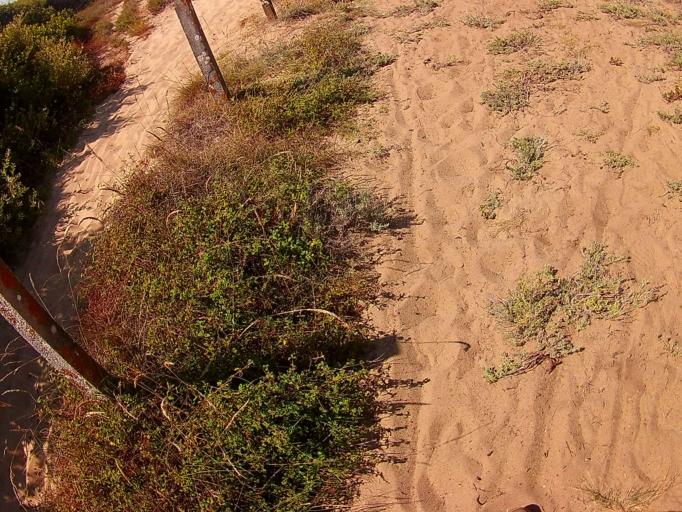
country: FR
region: Aquitaine
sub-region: Departement des Landes
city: Labenne
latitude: 43.6062
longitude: -1.4650
